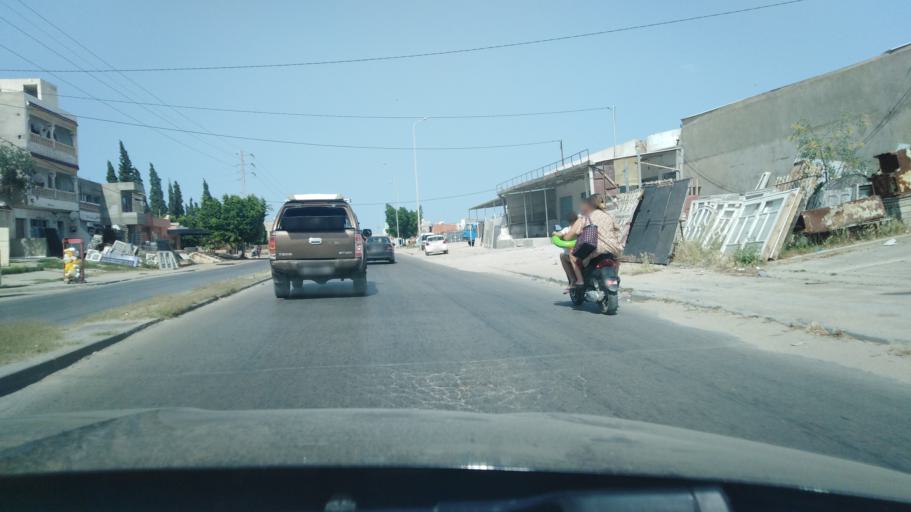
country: TN
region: Susah
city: Sousse
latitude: 35.7958
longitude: 10.6015
